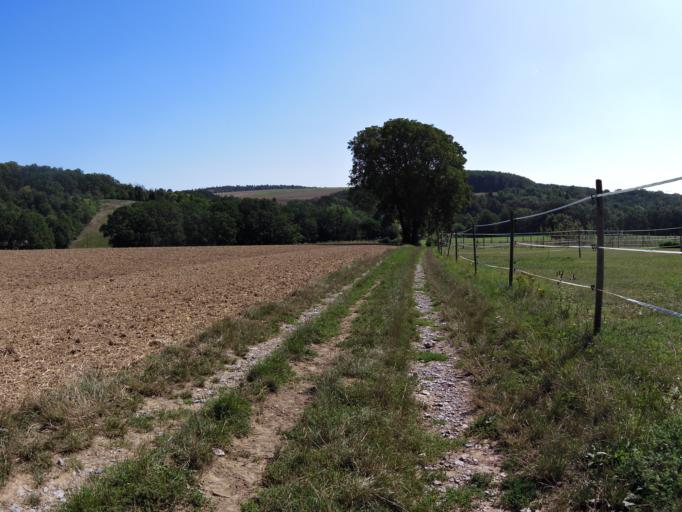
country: DE
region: Bavaria
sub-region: Regierungsbezirk Unterfranken
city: Veitshochheim
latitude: 49.8433
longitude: 9.8859
